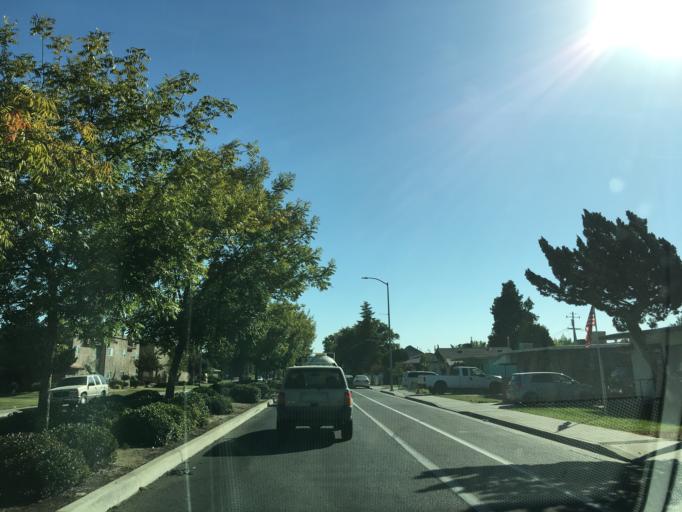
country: US
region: California
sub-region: Madera County
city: Madera
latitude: 36.9745
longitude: -120.0721
